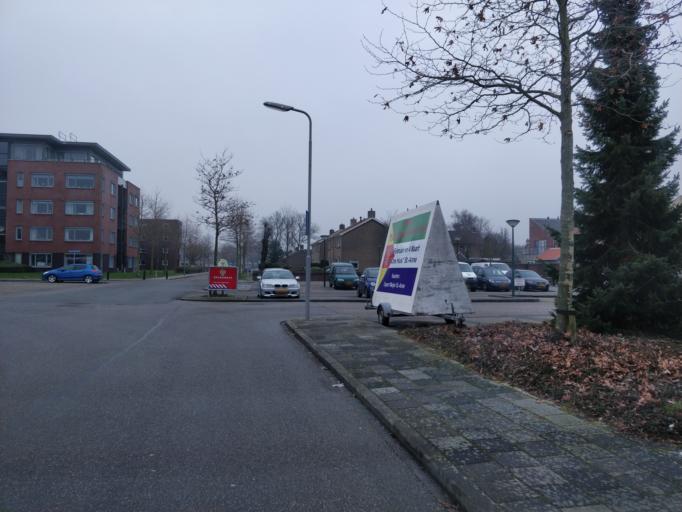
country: NL
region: Friesland
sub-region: Gemeente Het Bildt
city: Sint Annaparochie
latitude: 53.2745
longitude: 5.6581
